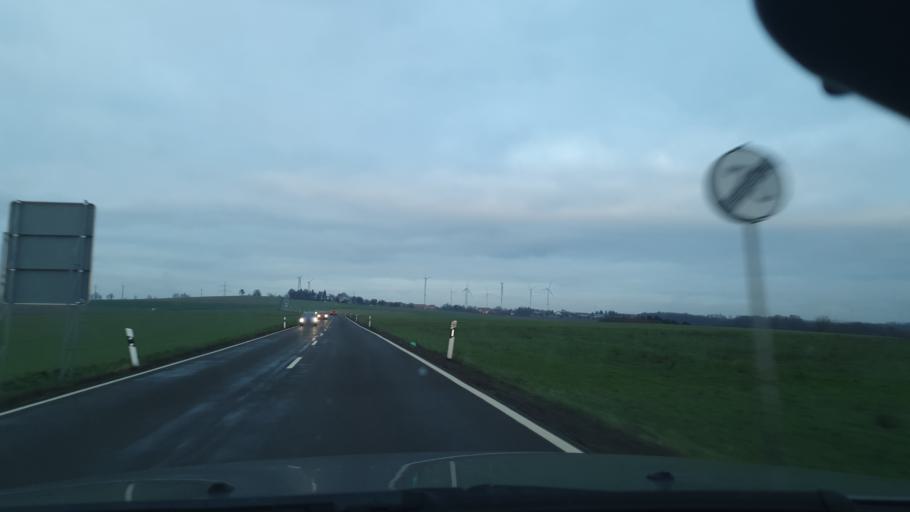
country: DE
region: Rheinland-Pfalz
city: Kashofen
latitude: 49.3347
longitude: 7.4271
